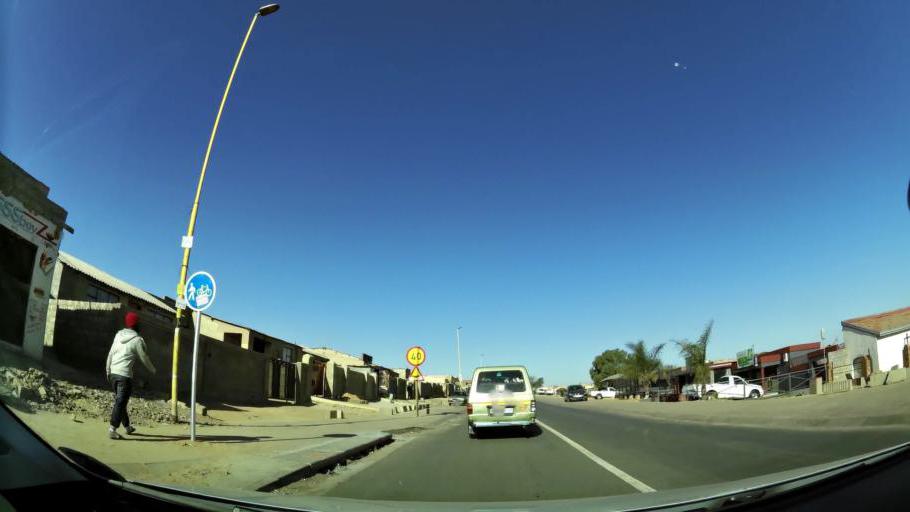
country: ZA
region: Gauteng
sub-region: Ekurhuleni Metropolitan Municipality
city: Tembisa
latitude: -26.0258
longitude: 28.2098
